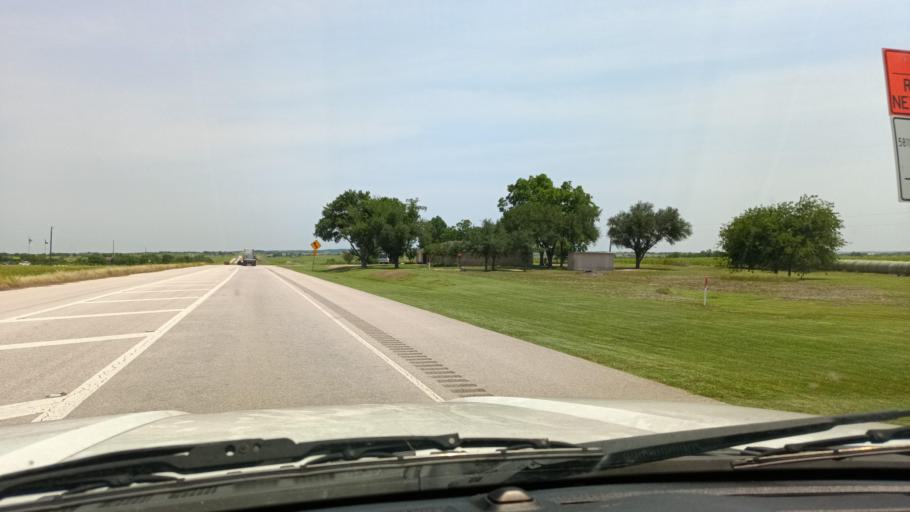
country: US
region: Texas
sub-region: Bell County
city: Little River-Academy
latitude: 30.9951
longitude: -97.2862
